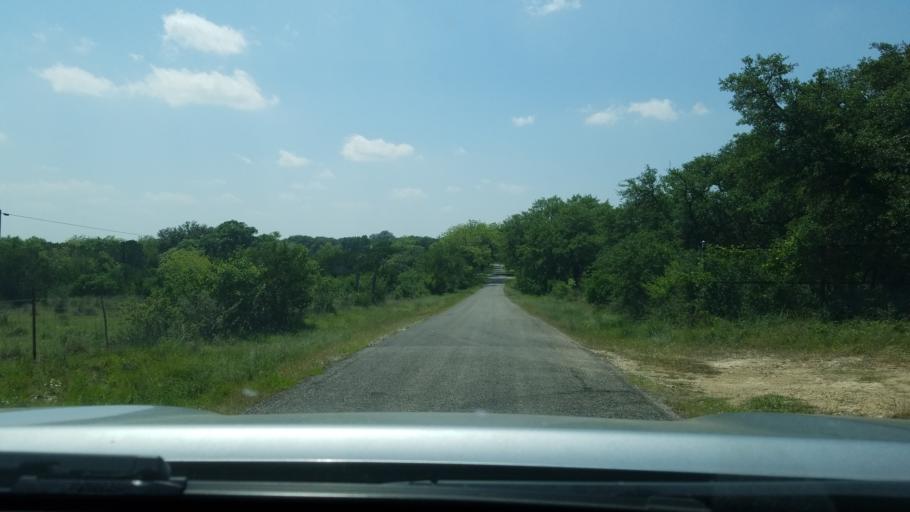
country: US
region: Texas
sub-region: Blanco County
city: Blanco
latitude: 29.9876
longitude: -98.5355
